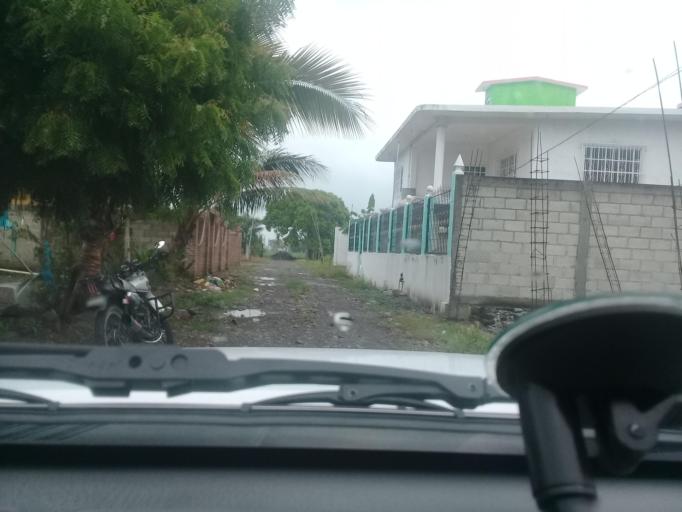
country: MX
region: Veracruz
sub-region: La Antigua
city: Nicolas Blanco (San Pancho)
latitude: 19.3392
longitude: -96.3610
